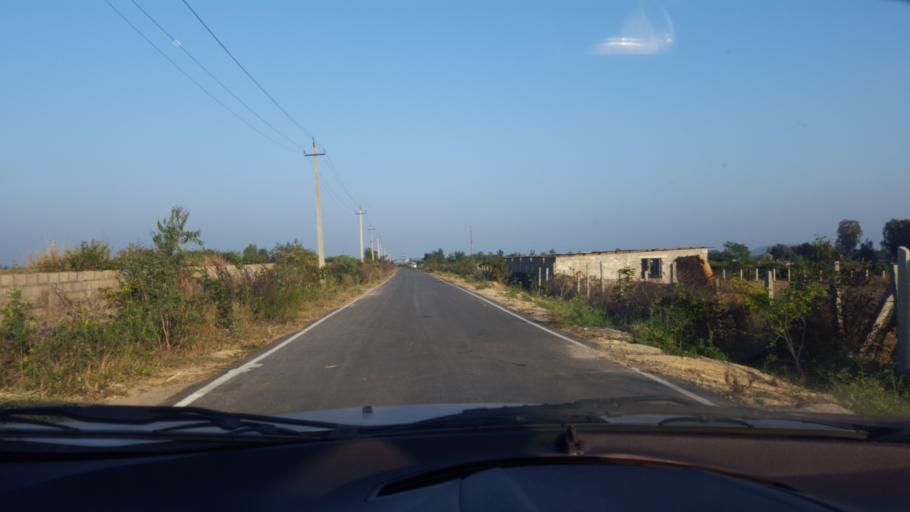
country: IN
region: Karnataka
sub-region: Bangalore Urban
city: Yelahanka
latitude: 13.1897
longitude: 77.6016
